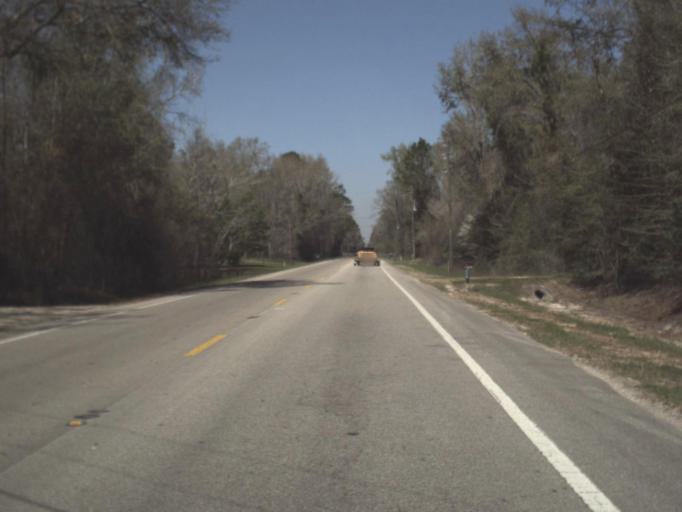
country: US
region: Florida
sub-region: Leon County
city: Woodville
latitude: 30.2516
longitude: -84.2341
